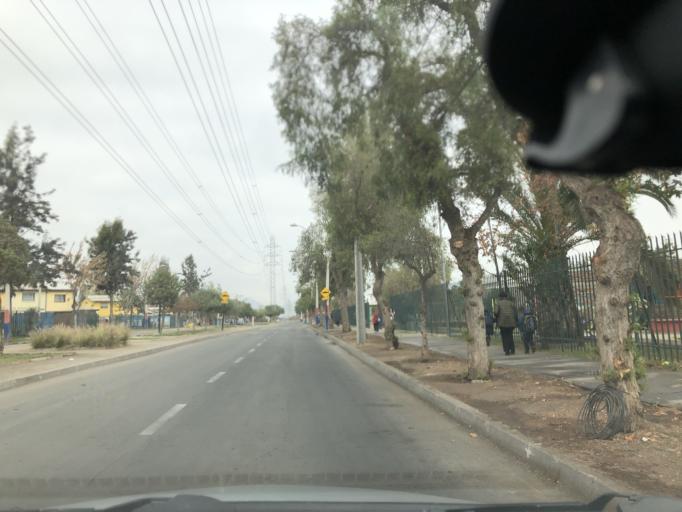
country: CL
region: Santiago Metropolitan
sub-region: Provincia de Cordillera
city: Puente Alto
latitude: -33.5951
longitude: -70.6016
